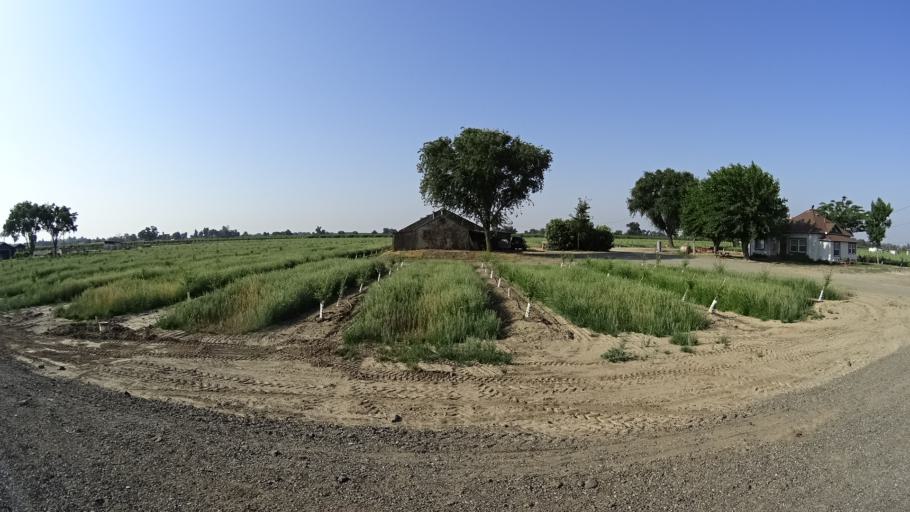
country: US
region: California
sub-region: Fresno County
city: Riverdale
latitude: 36.3584
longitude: -119.8490
